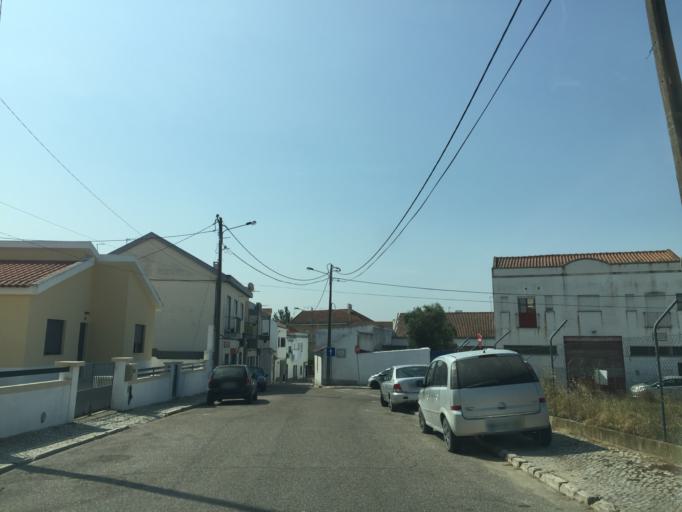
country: PT
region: Setubal
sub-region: Setubal
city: Setubal
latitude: 38.5847
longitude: -8.6902
